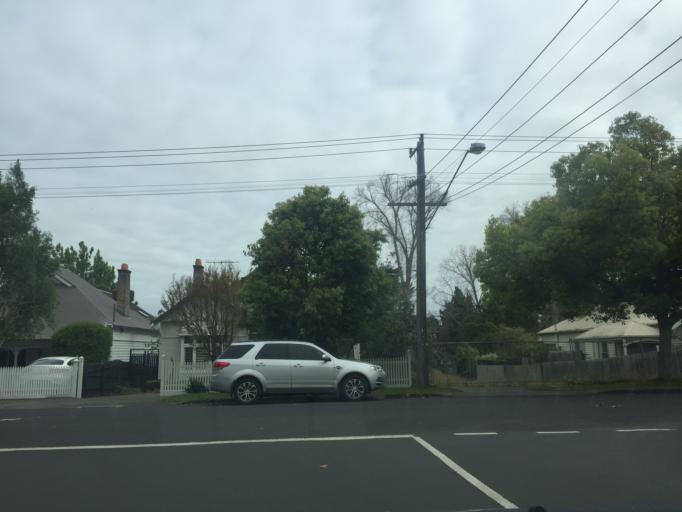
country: AU
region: Victoria
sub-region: Boroondara
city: Hawthorn East
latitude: -37.8189
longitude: 145.0557
